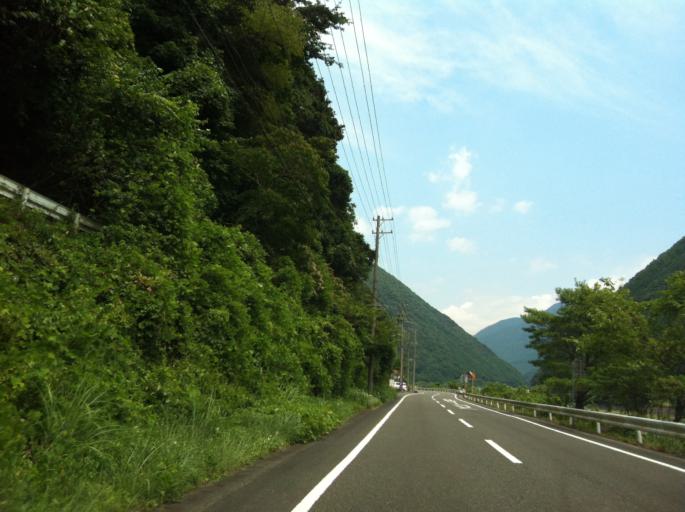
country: JP
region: Shizuoka
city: Shizuoka-shi
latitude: 35.1674
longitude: 138.3613
